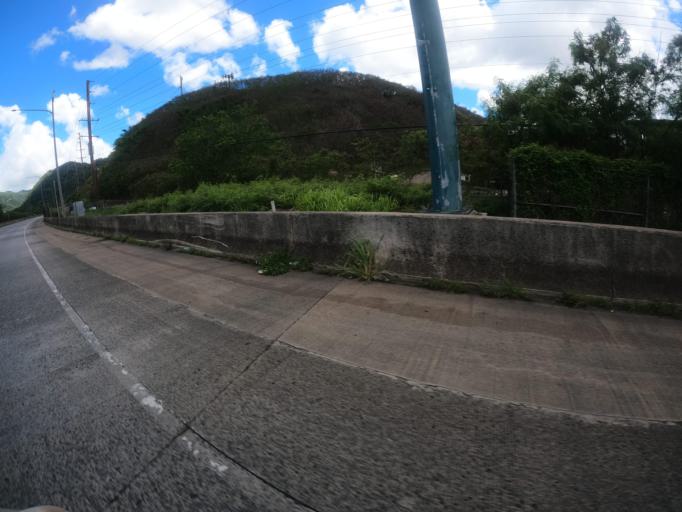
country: US
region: Hawaii
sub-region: Honolulu County
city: Halawa Heights
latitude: 21.3784
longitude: -157.9066
